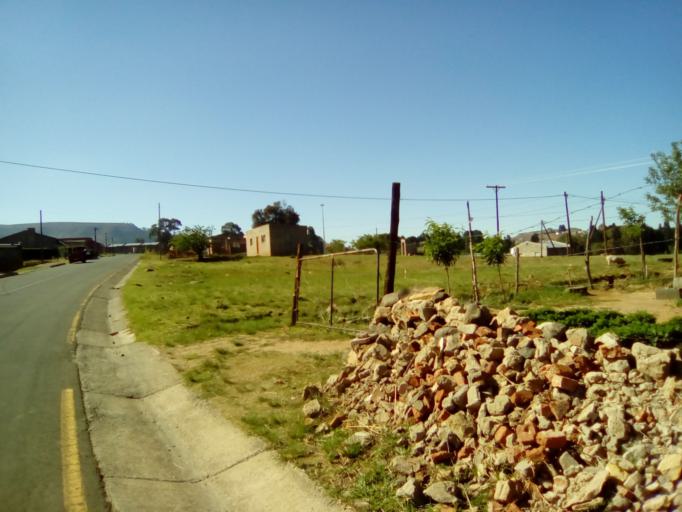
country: LS
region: Qacha's Nek
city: Qacha's Nek
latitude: -30.1060
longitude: 28.6808
